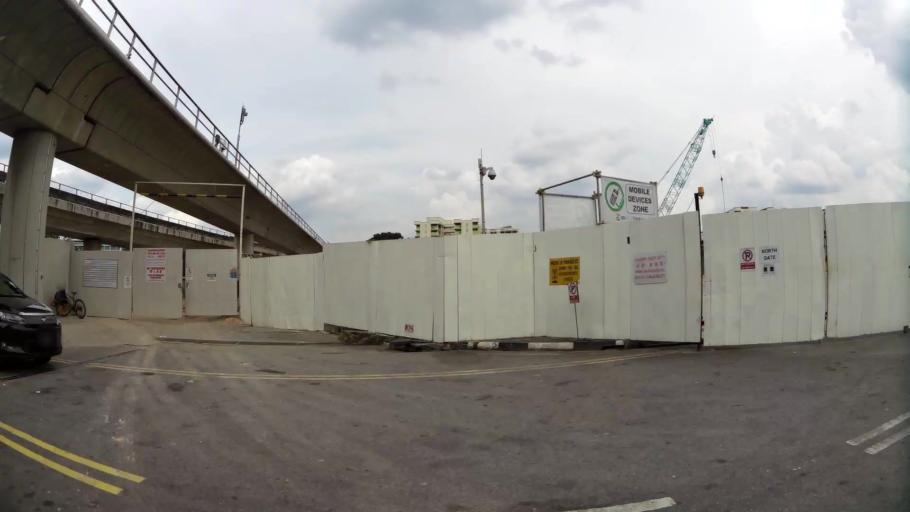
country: MY
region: Johor
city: Johor Bahru
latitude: 1.4371
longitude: 103.7874
